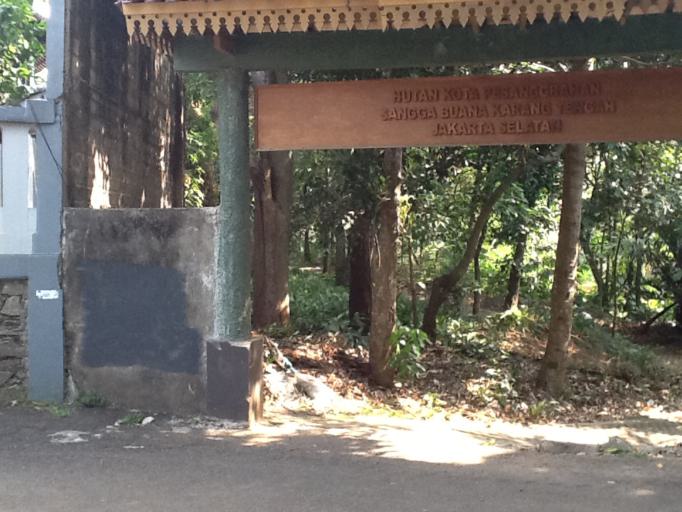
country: ID
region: West Java
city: Pamulang
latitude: -6.3121
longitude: 106.7782
